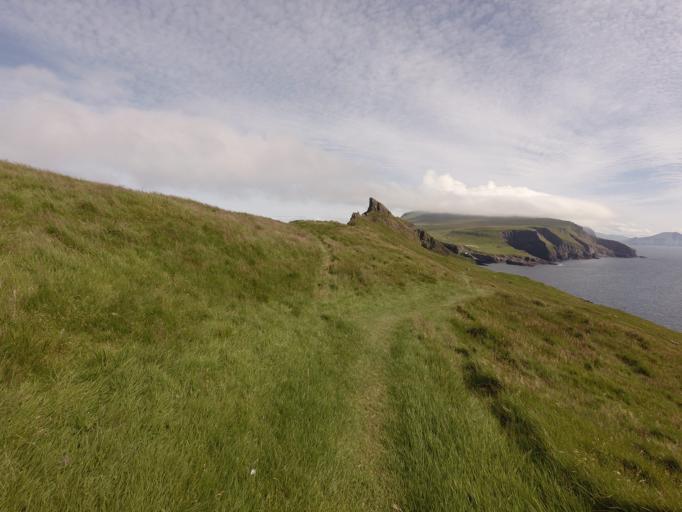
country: FO
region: Vagar
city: Sorvagur
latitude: 62.1002
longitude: -7.6709
